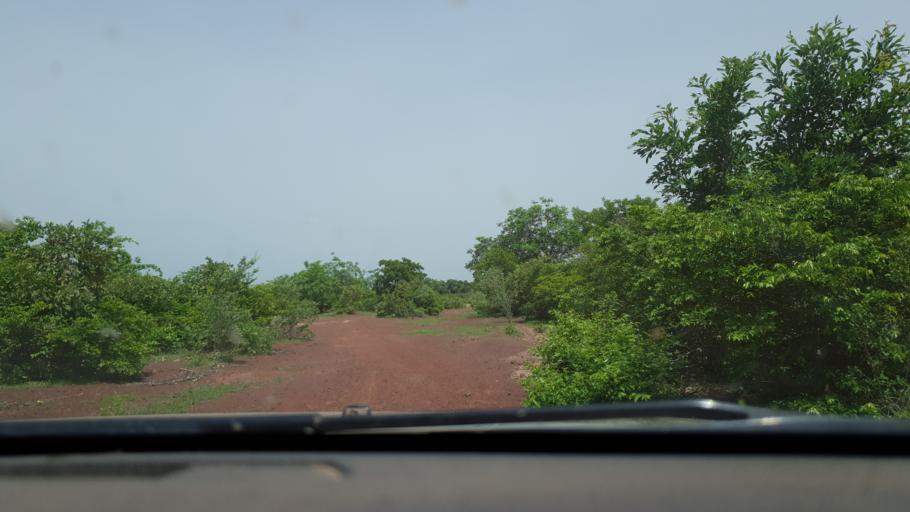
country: ML
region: Koulikoro
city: Koulikoro
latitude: 12.6667
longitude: -7.2363
